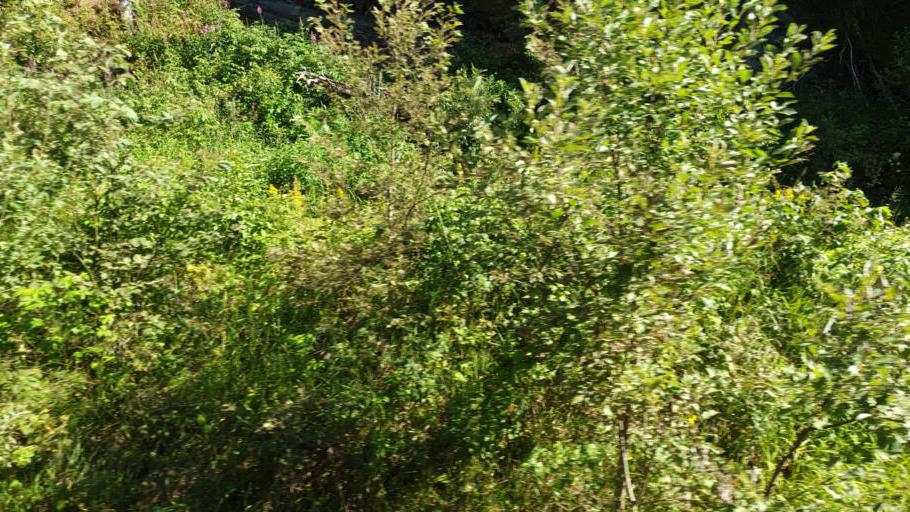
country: NO
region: Sor-Trondelag
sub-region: Meldal
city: Meldal
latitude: 63.1823
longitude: 9.7693
